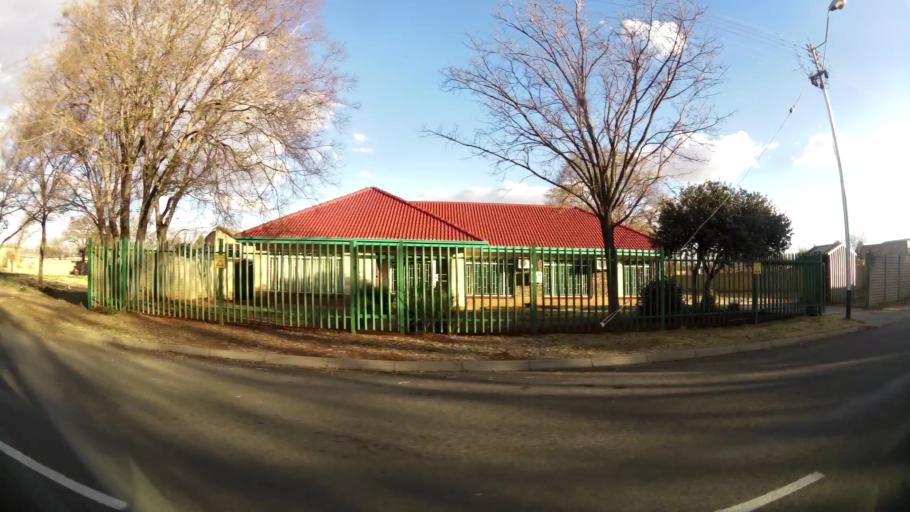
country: ZA
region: North-West
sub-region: Dr Kenneth Kaunda District Municipality
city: Potchefstroom
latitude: -26.7165
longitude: 27.1004
